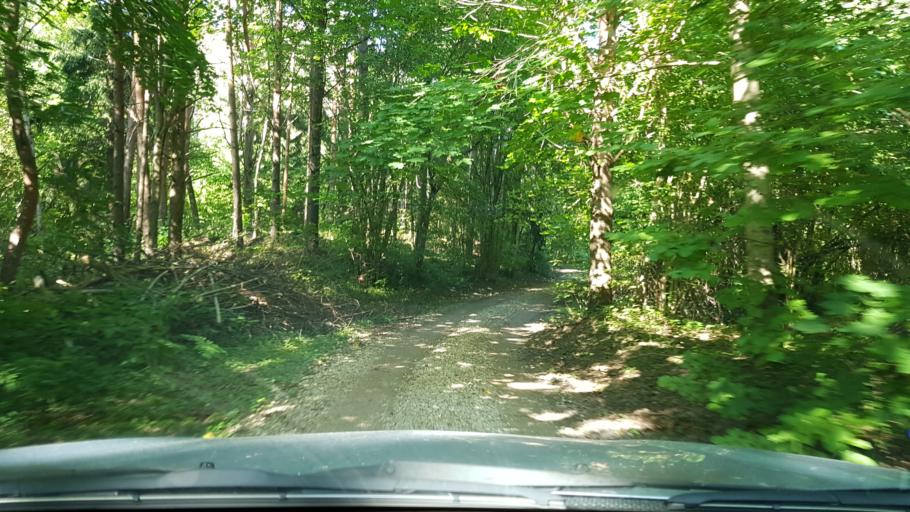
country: EE
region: Ida-Virumaa
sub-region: Sillamaee linn
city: Sillamae
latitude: 59.3978
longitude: 27.8787
